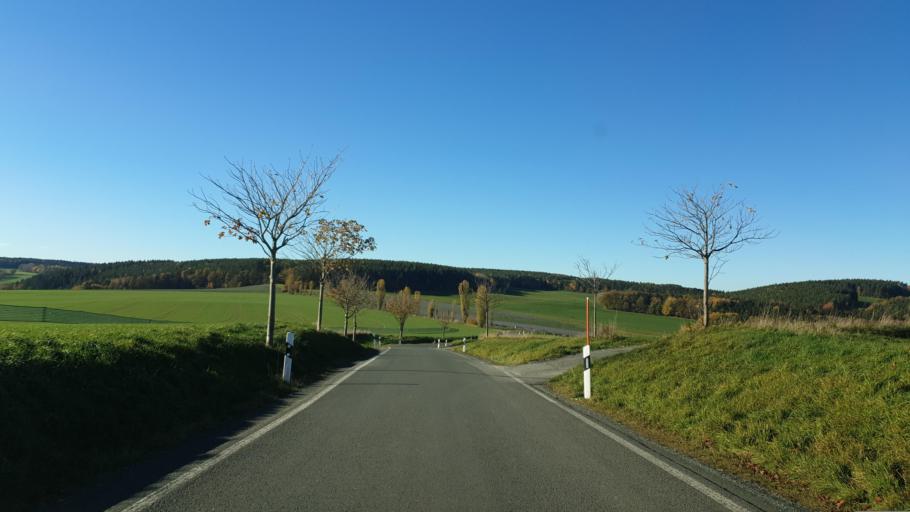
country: DE
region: Saxony
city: Elsterberg
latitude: 50.6150
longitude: 12.1312
